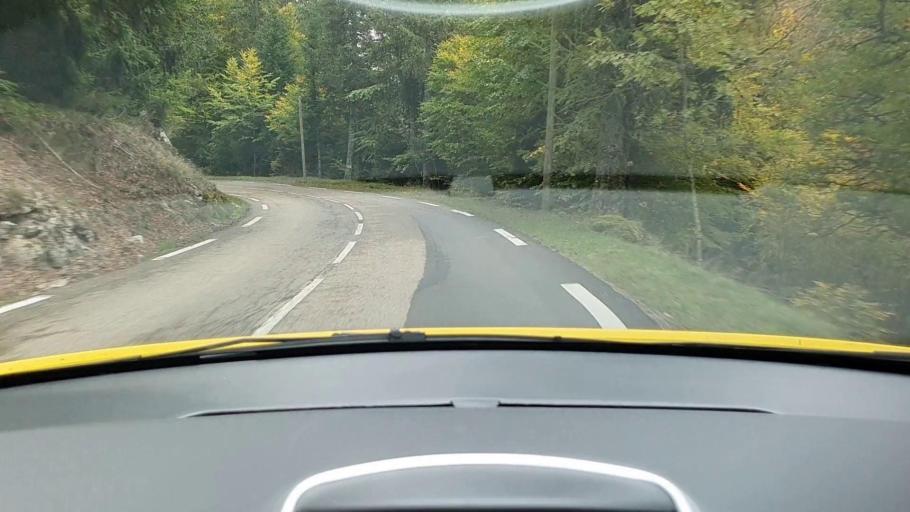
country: FR
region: Languedoc-Roussillon
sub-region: Departement de la Lozere
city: Meyrueis
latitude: 44.1045
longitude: 3.4980
